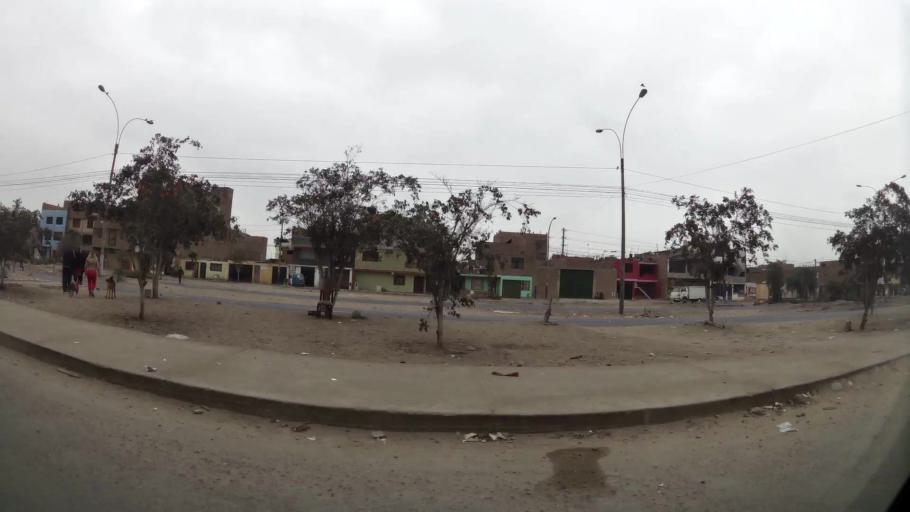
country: PE
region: Lima
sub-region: Lima
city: Independencia
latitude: -11.9695
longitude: -77.0606
